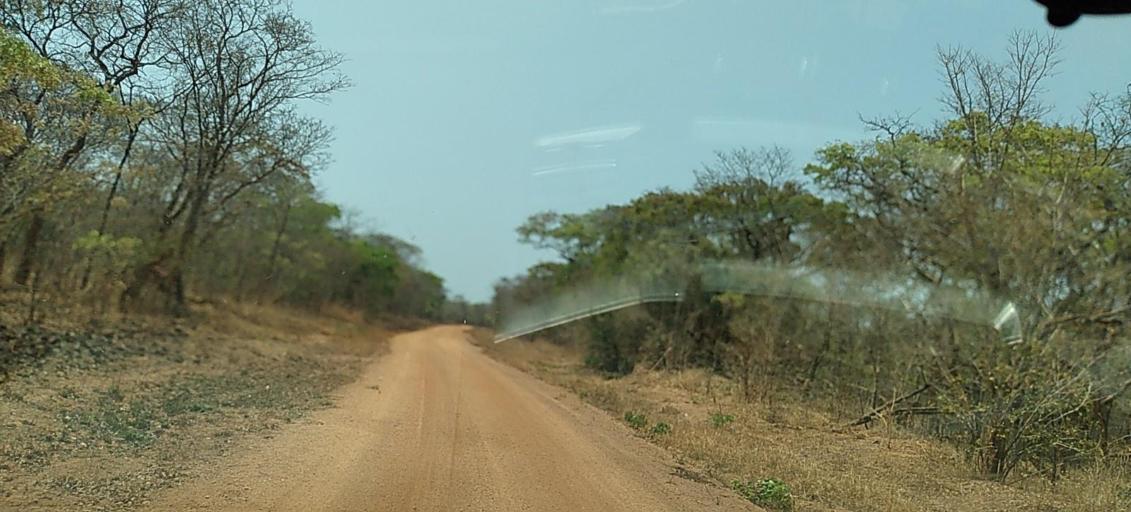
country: ZM
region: Central
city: Mumbwa
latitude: -14.2634
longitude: 26.5131
